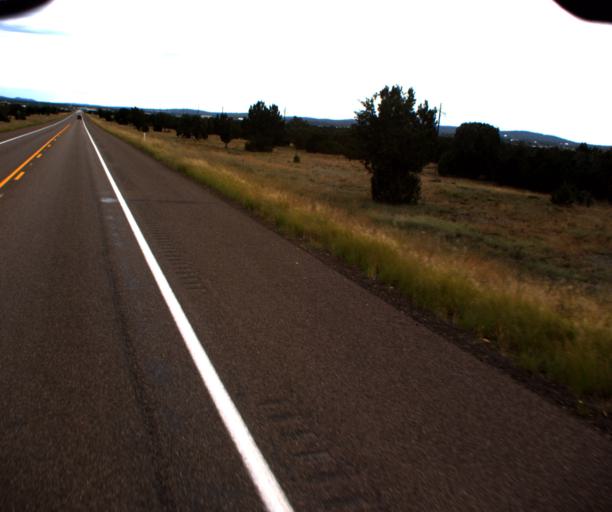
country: US
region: Arizona
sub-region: Navajo County
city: Show Low
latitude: 34.2855
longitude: -110.0292
